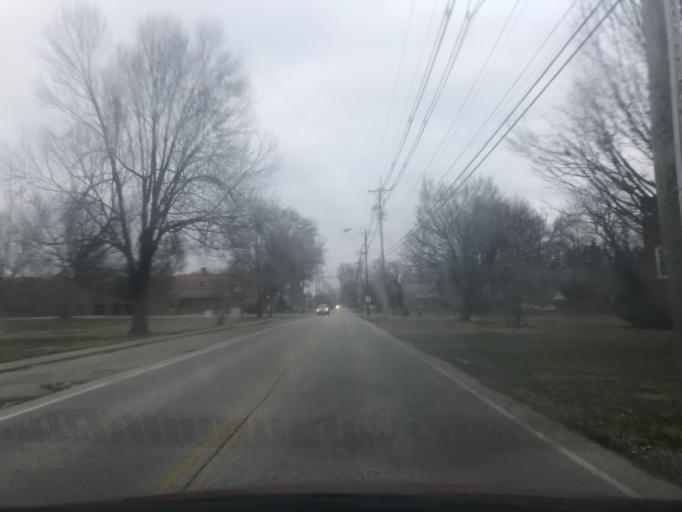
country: US
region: Kentucky
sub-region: Jefferson County
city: Audubon Park
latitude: 38.2076
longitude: -85.7304
